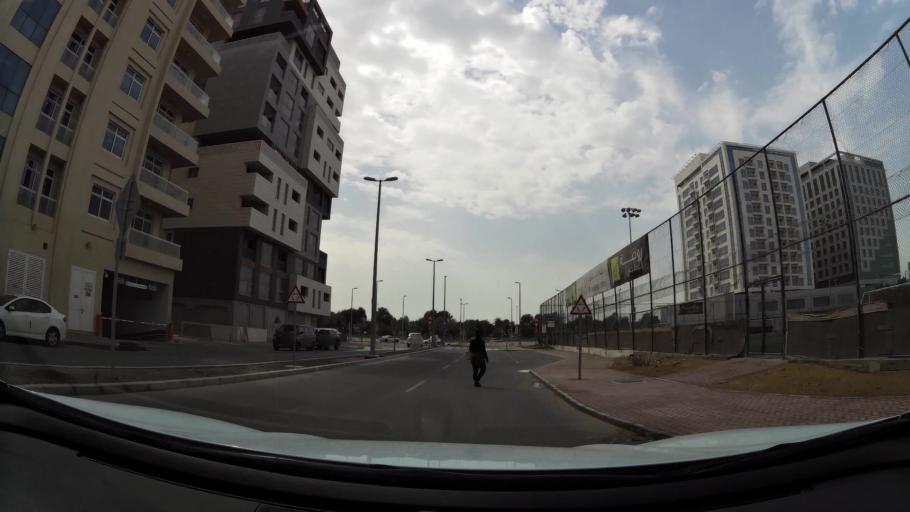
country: AE
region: Abu Dhabi
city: Abu Dhabi
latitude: 24.4208
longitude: 54.4619
